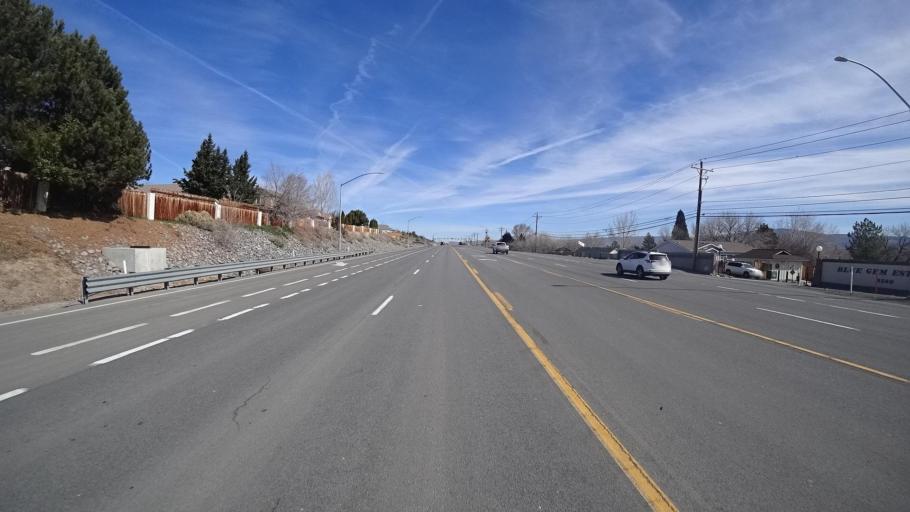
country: US
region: Nevada
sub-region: Washoe County
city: Sun Valley
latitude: 39.5908
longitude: -119.7401
